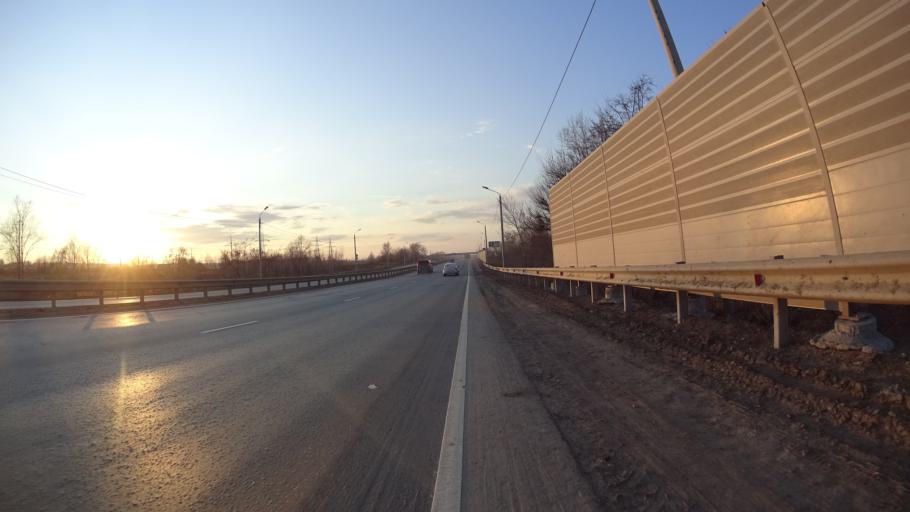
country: RU
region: Chelyabinsk
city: Novosineglazovskiy
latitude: 55.0575
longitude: 61.4054
